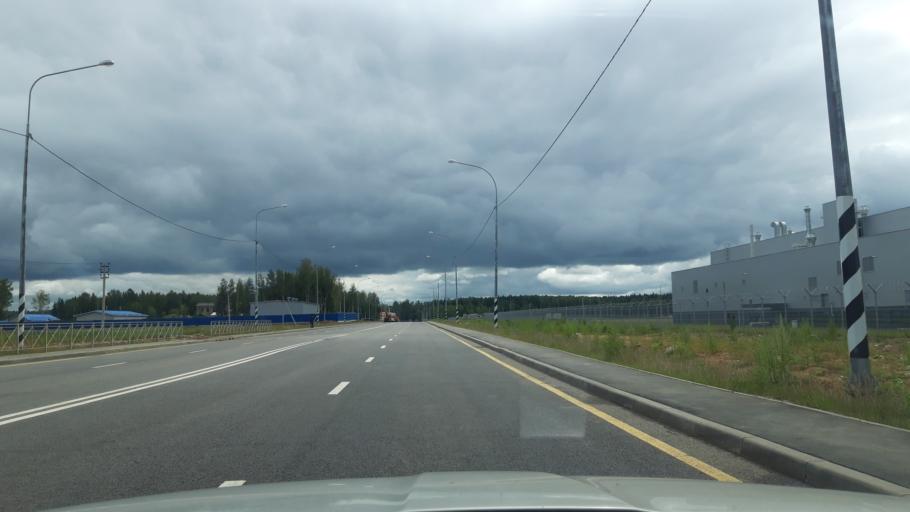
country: RU
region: Moskovskaya
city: Lozhki
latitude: 56.0852
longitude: 37.0837
